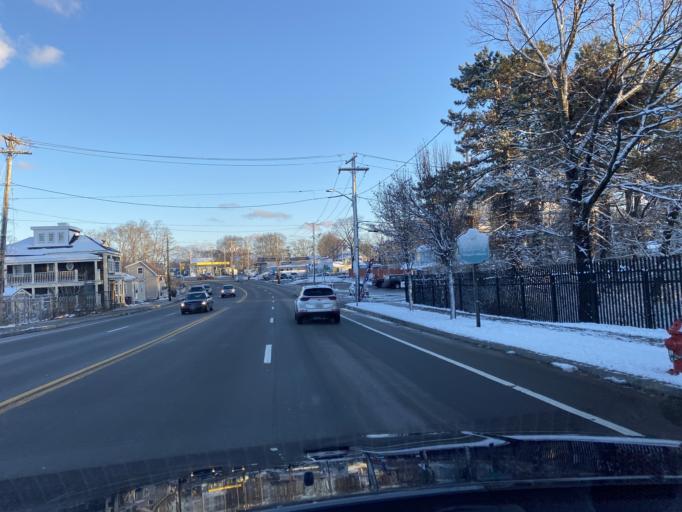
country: US
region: Massachusetts
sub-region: Norfolk County
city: Weymouth
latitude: 42.2433
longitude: -70.9628
